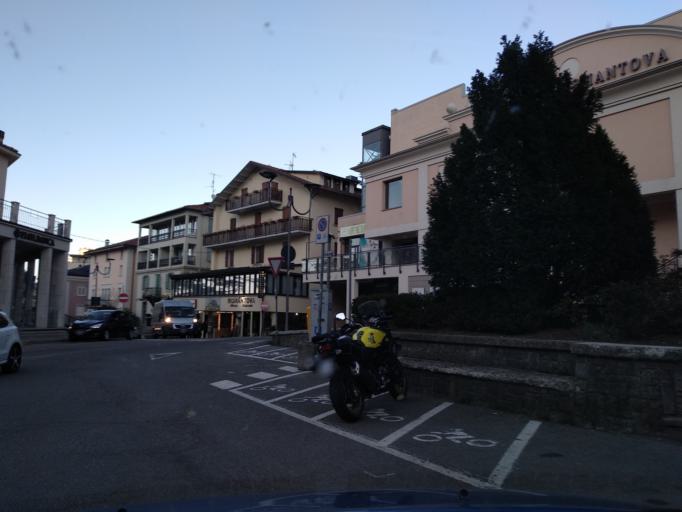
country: IT
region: Emilia-Romagna
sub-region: Provincia di Reggio Emilia
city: Castelnovo ne'Monti
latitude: 44.4344
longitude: 10.4008
